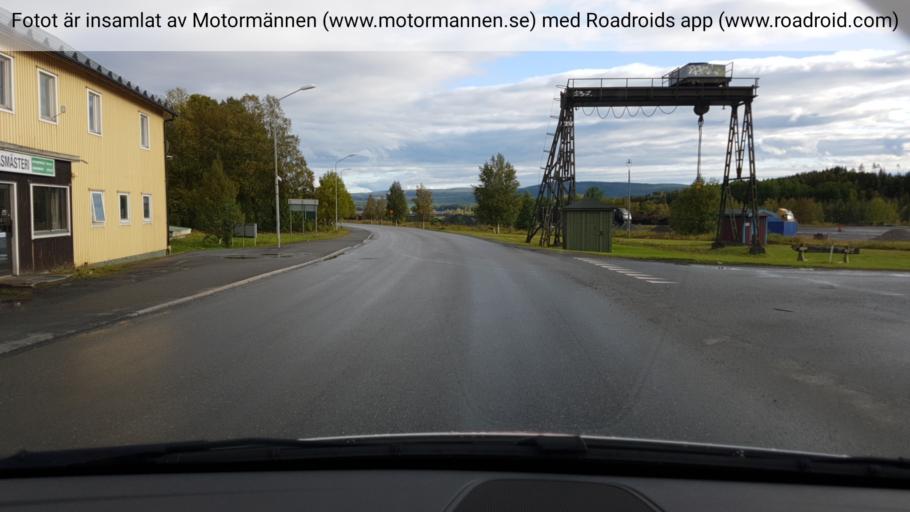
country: SE
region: Jaemtland
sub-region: Are Kommun
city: Jarpen
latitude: 63.3549
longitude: 13.4422
